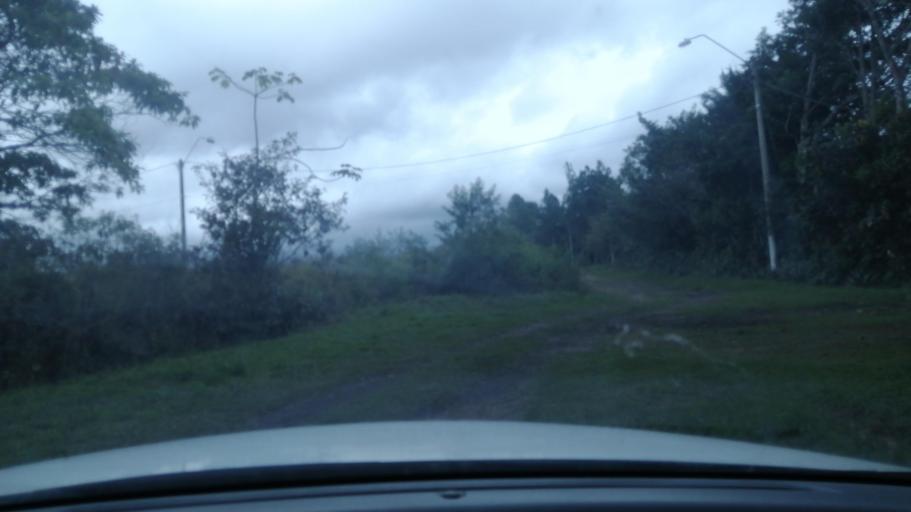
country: PA
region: Chiriqui
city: Potrerillos Arriba
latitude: 8.6849
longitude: -82.4554
